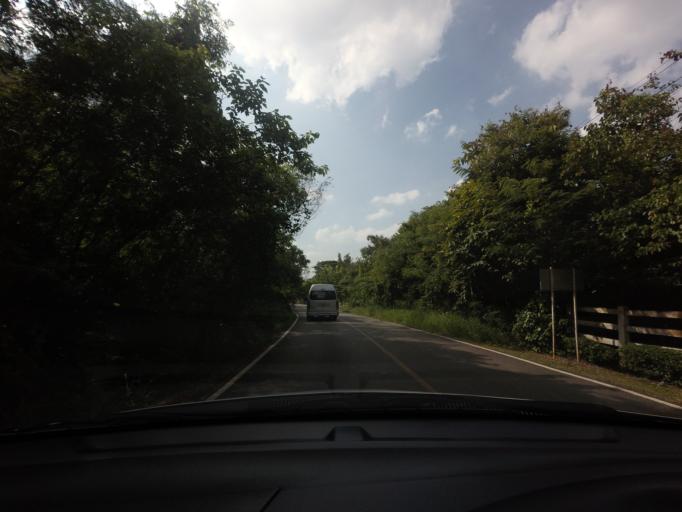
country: TH
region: Nakhon Ratchasima
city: Pak Chong
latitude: 14.5295
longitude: 101.3937
